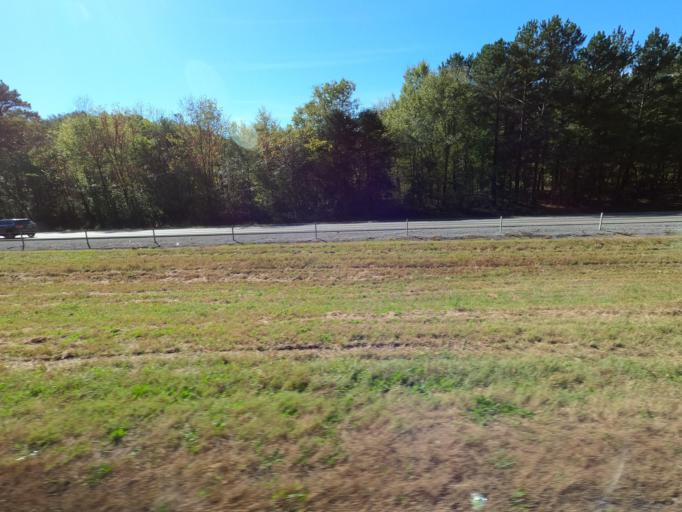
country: US
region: Tennessee
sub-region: Cheatham County
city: Pegram
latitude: 36.0874
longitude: -87.0538
